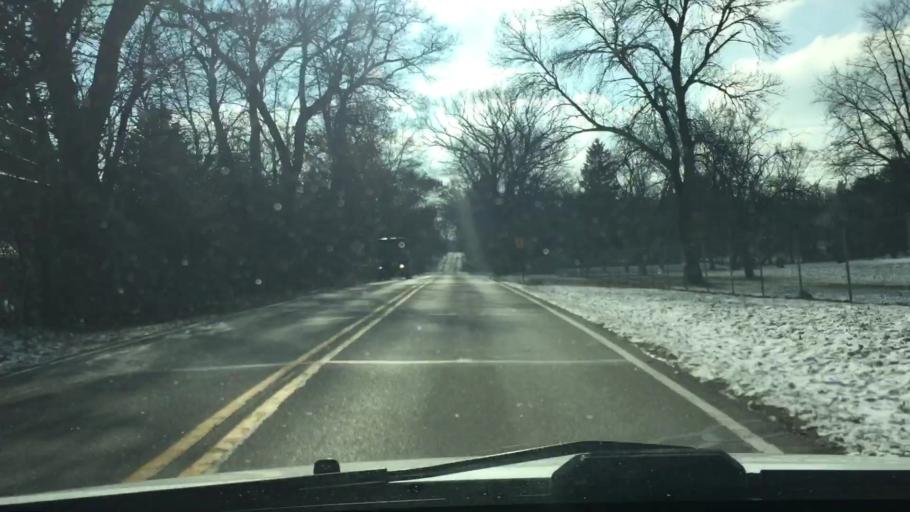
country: US
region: Wisconsin
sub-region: Waukesha County
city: Waukesha
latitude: 42.9829
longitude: -88.2872
